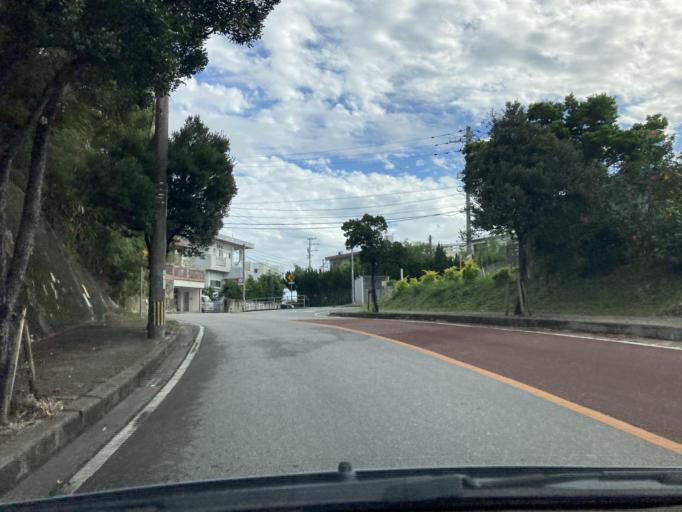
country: JP
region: Okinawa
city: Tomigusuku
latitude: 26.1809
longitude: 127.7461
